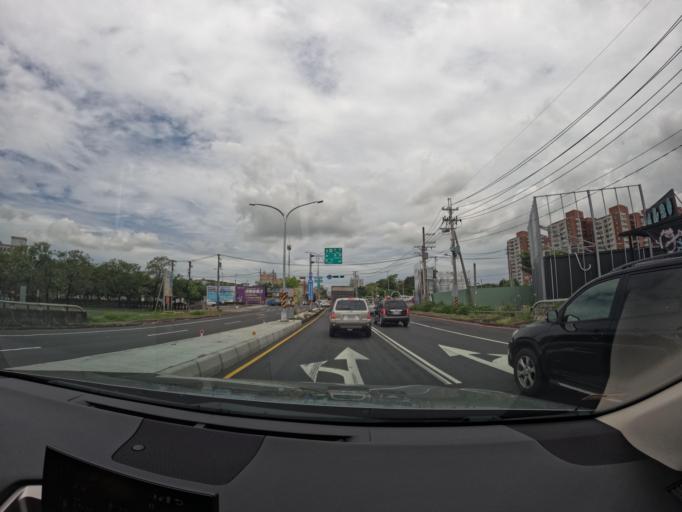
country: TW
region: Kaohsiung
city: Kaohsiung
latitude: 22.7846
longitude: 120.2979
